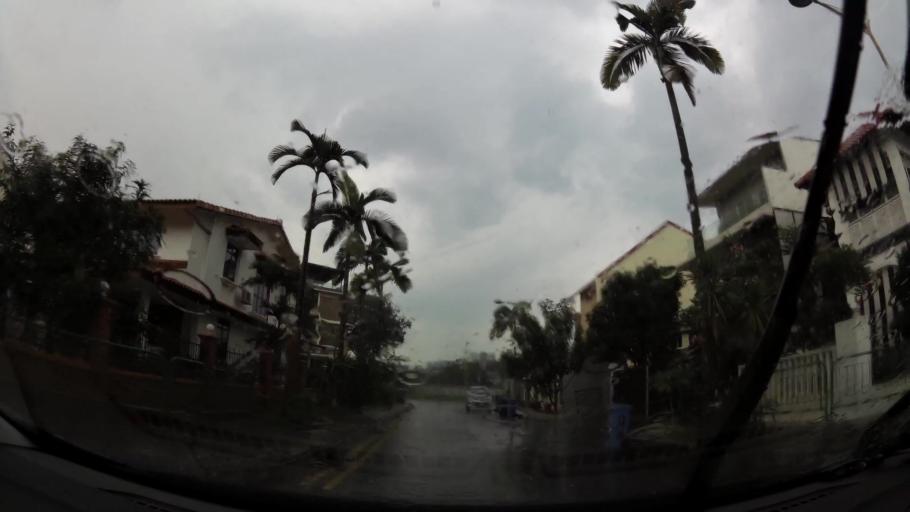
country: SG
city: Singapore
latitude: 1.3345
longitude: 103.9442
